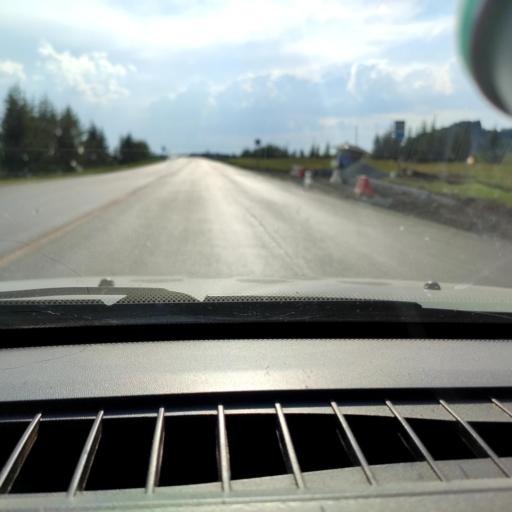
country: RU
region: Udmurtiya
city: Debesy
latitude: 57.6946
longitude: 53.9915
